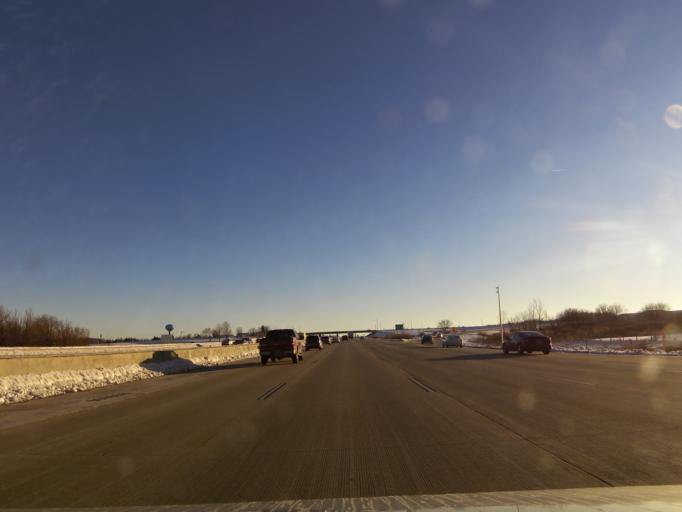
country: US
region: Wisconsin
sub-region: Kenosha County
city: Pleasant Prairie
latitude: 42.5294
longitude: -87.9523
